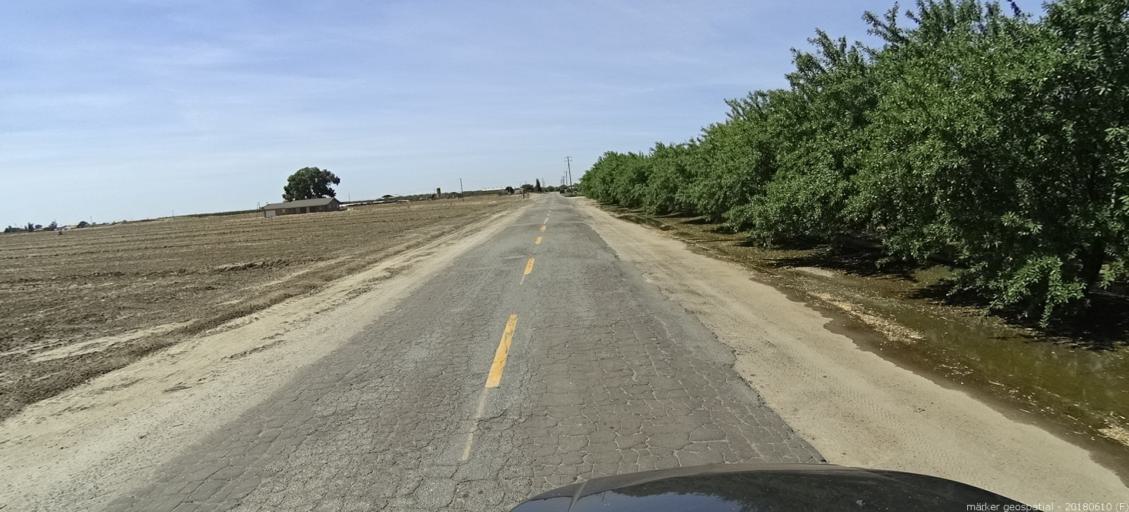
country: US
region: California
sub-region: Madera County
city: Chowchilla
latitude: 37.0157
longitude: -120.3557
